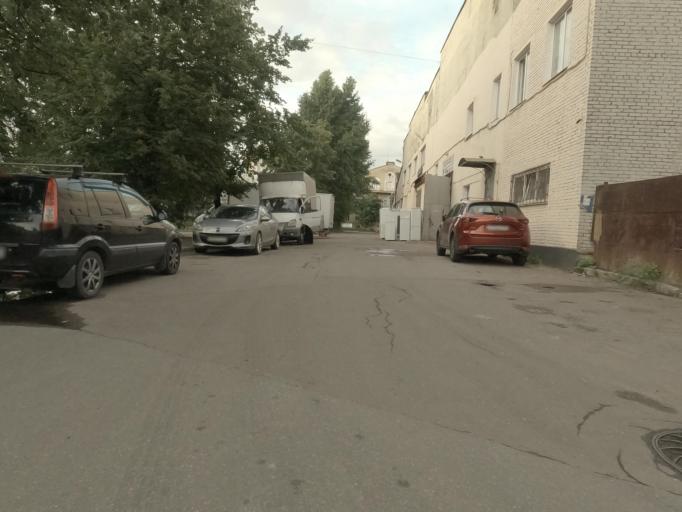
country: RU
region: St.-Petersburg
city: Avtovo
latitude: 59.8852
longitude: 30.2808
